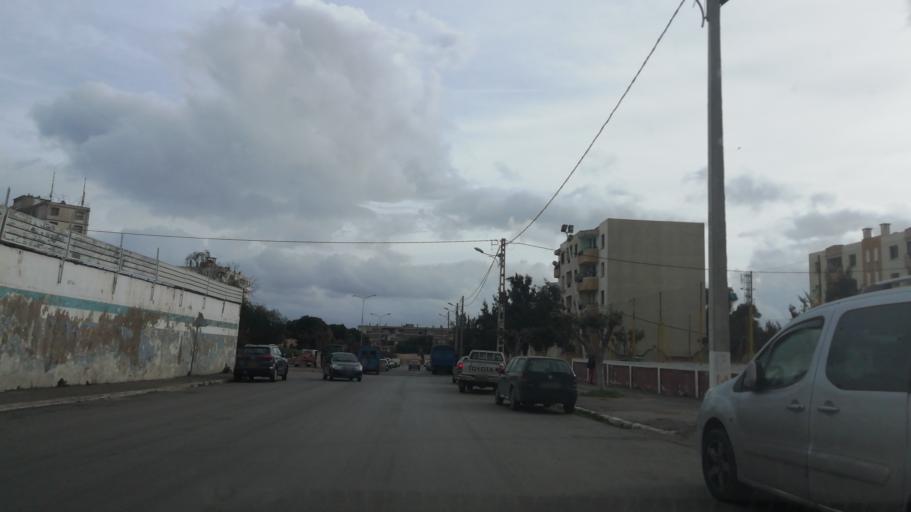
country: DZ
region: Oran
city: Oran
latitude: 35.6828
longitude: -0.6414
